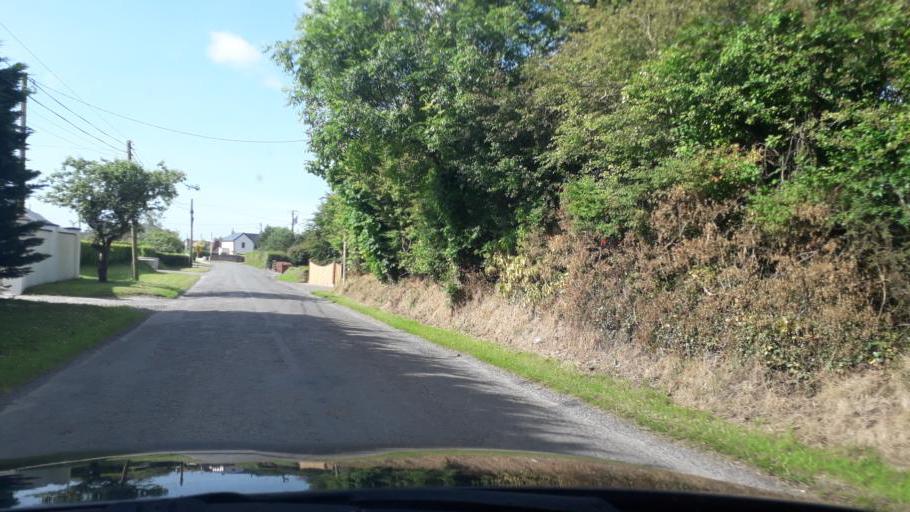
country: IE
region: Leinster
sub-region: Loch Garman
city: Loch Garman
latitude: 52.2455
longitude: -6.5504
